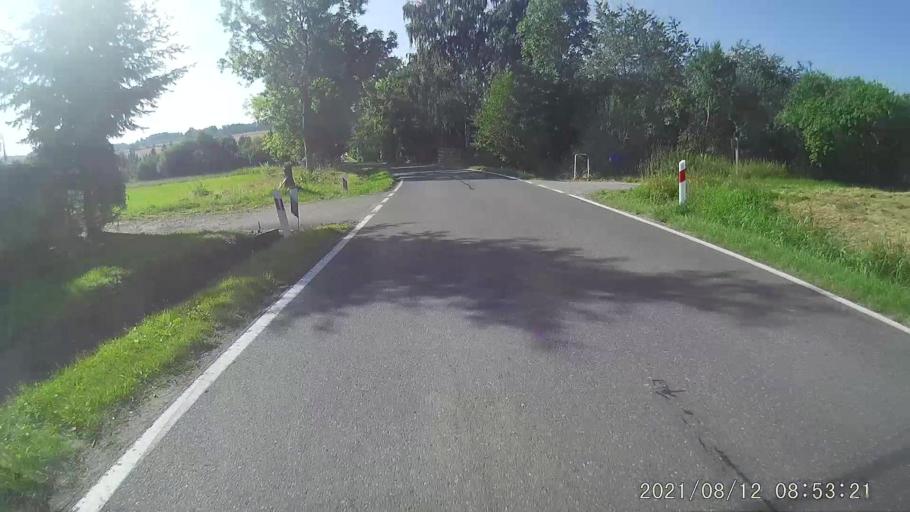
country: PL
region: Lower Silesian Voivodeship
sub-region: Powiat klodzki
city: Polanica-Zdroj
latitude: 50.4360
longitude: 16.5030
